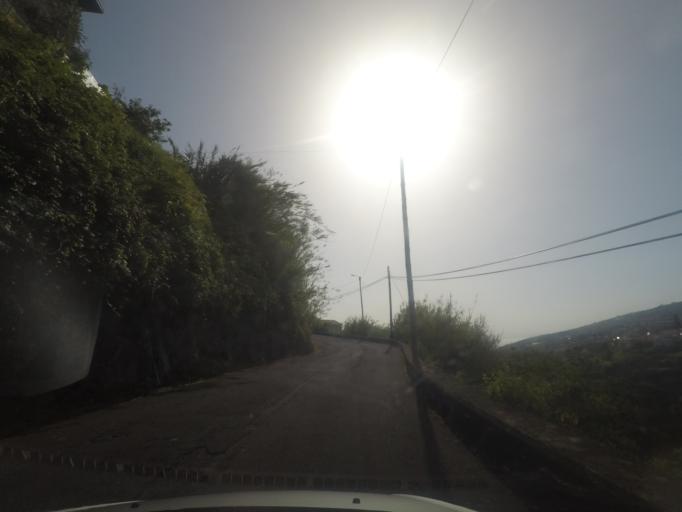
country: PT
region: Madeira
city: Calheta
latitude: 32.7269
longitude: -17.1671
